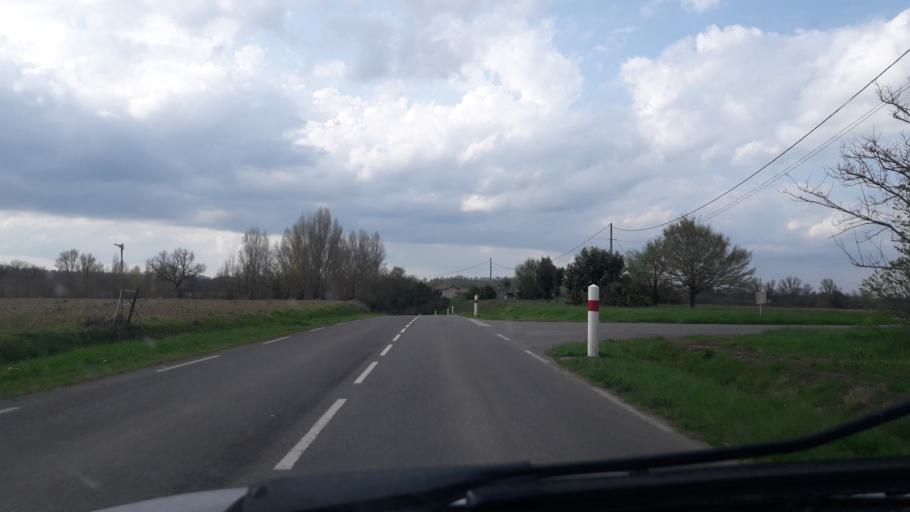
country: FR
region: Midi-Pyrenees
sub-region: Departement de la Haute-Garonne
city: Rieux-Volvestre
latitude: 43.2652
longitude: 1.2080
